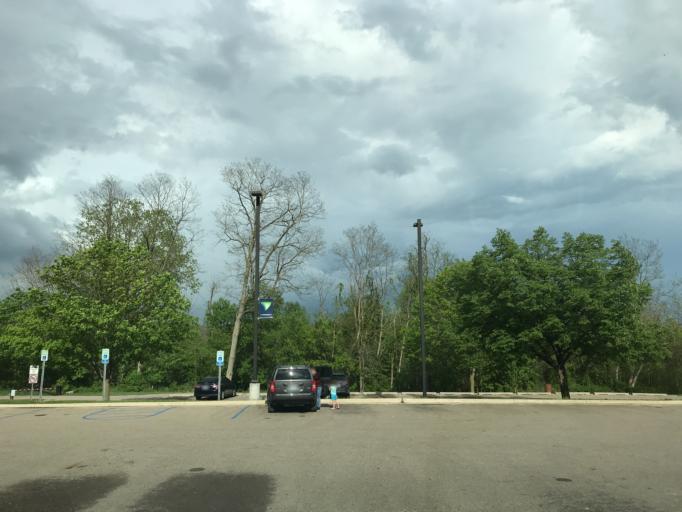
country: US
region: Michigan
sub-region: Oakland County
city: Milford
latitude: 42.5509
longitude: -83.6346
